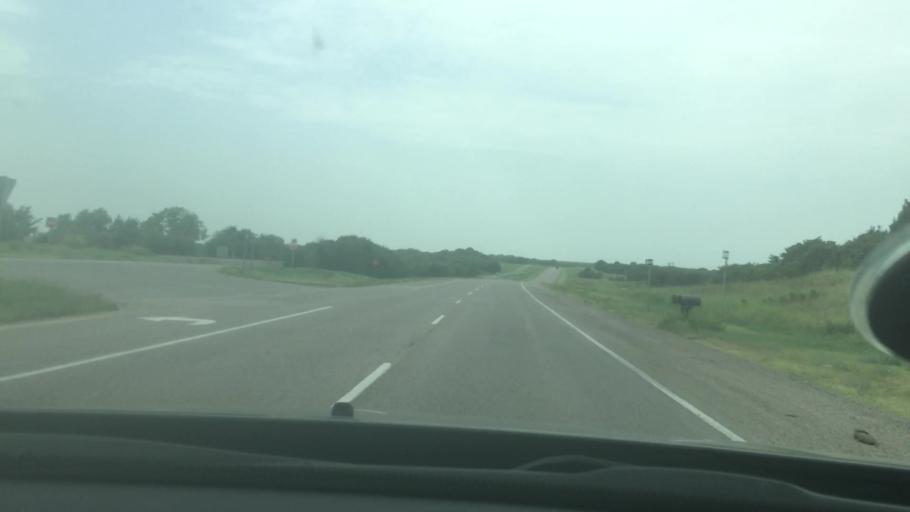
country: US
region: Oklahoma
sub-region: Pontotoc County
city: Ada
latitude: 34.7003
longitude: -96.7349
